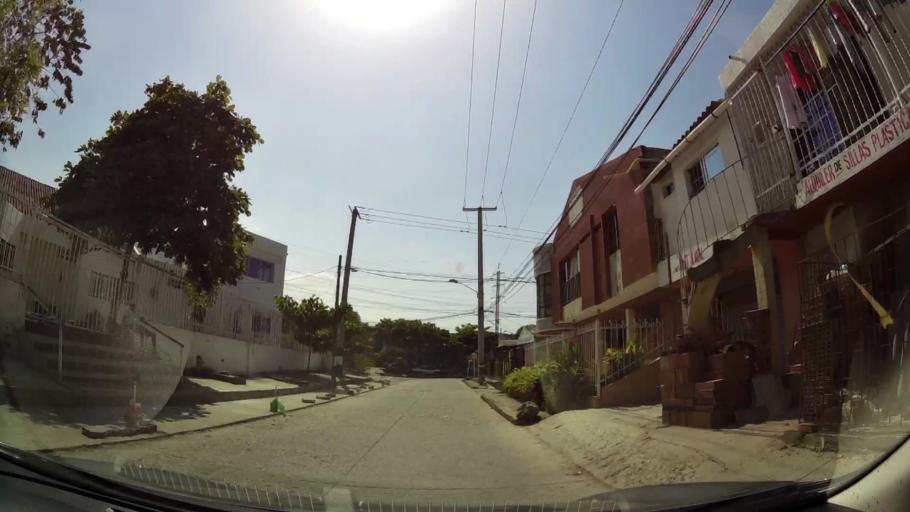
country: CO
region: Bolivar
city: Cartagena
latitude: 10.3779
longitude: -75.4671
